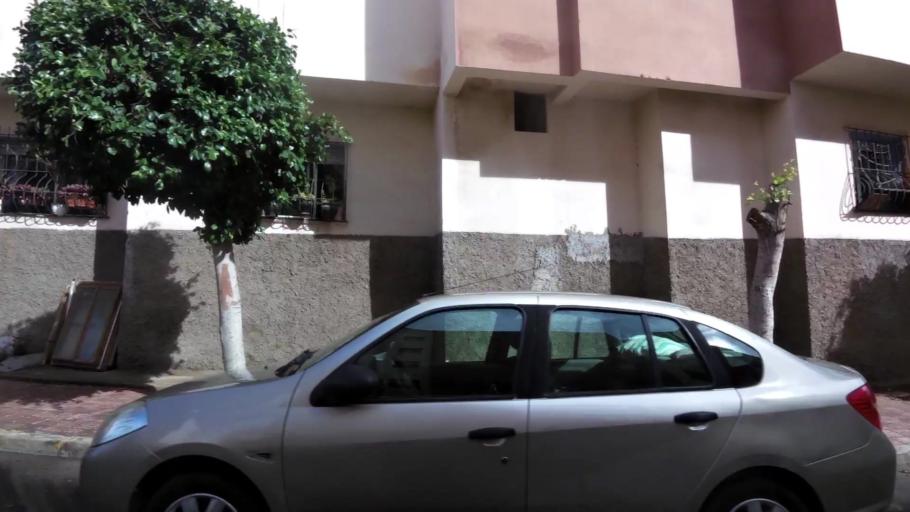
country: MA
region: Grand Casablanca
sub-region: Casablanca
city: Casablanca
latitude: 33.5629
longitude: -7.6739
